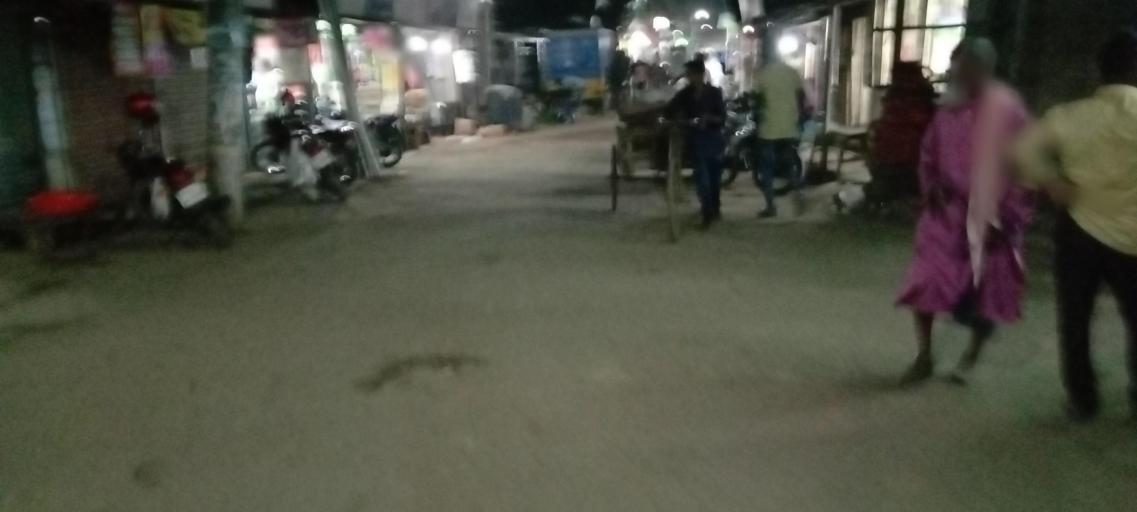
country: BD
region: Dhaka
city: Gafargaon
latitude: 24.4015
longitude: 90.3851
